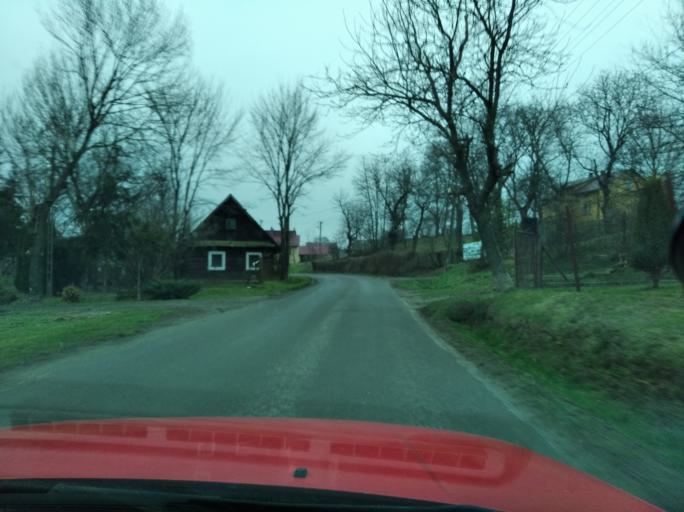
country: PL
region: Subcarpathian Voivodeship
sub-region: Powiat przeworski
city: Rozborz
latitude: 50.0639
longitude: 22.5386
